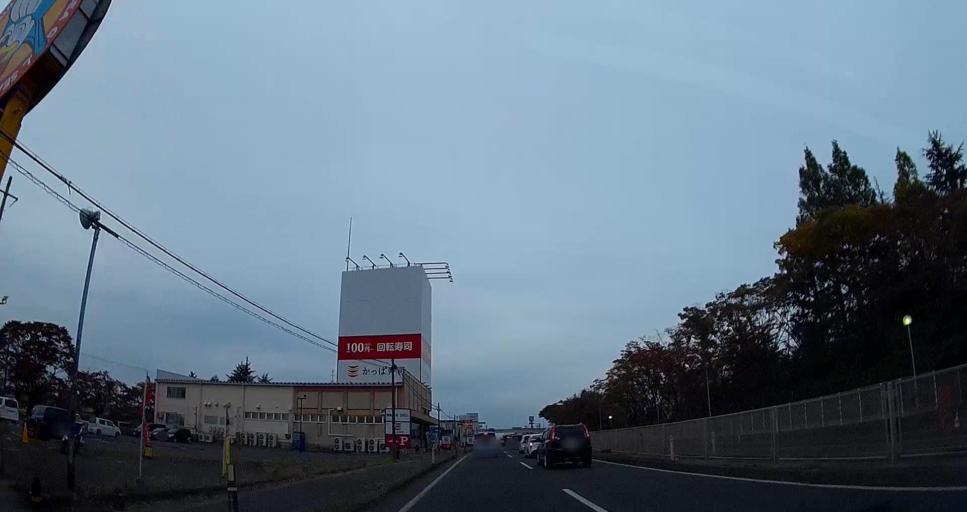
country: JP
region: Miyagi
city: Iwanuma
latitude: 38.1757
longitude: 140.8903
